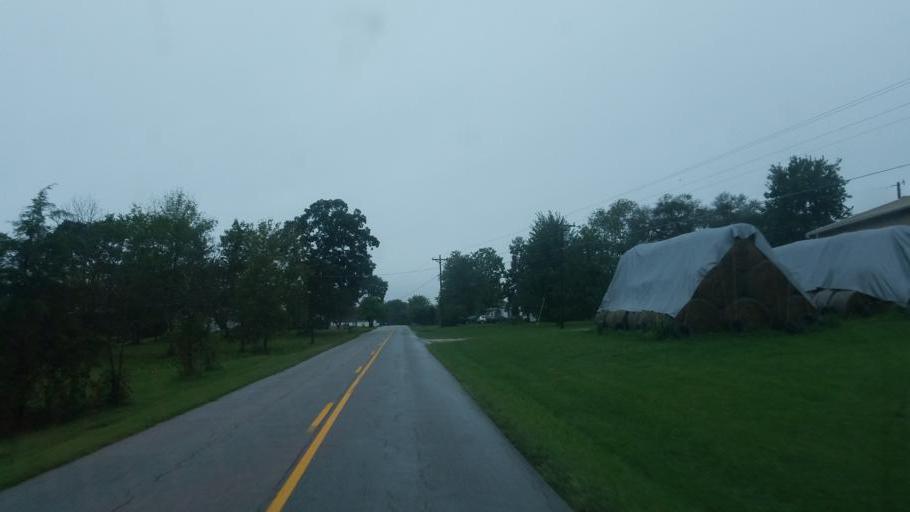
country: US
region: Kentucky
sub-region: Fleming County
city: Flemingsburg
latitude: 38.4032
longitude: -83.6240
